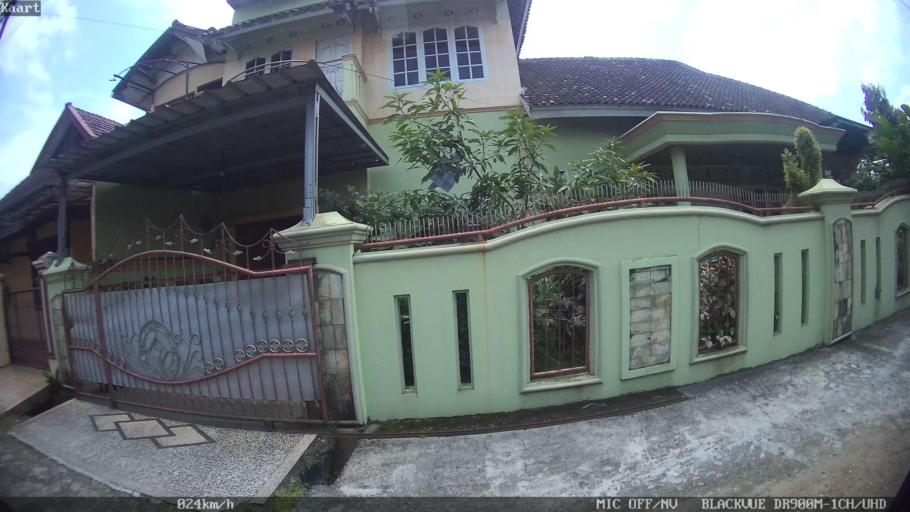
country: ID
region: Lampung
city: Kedaton
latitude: -5.3668
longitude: 105.3036
